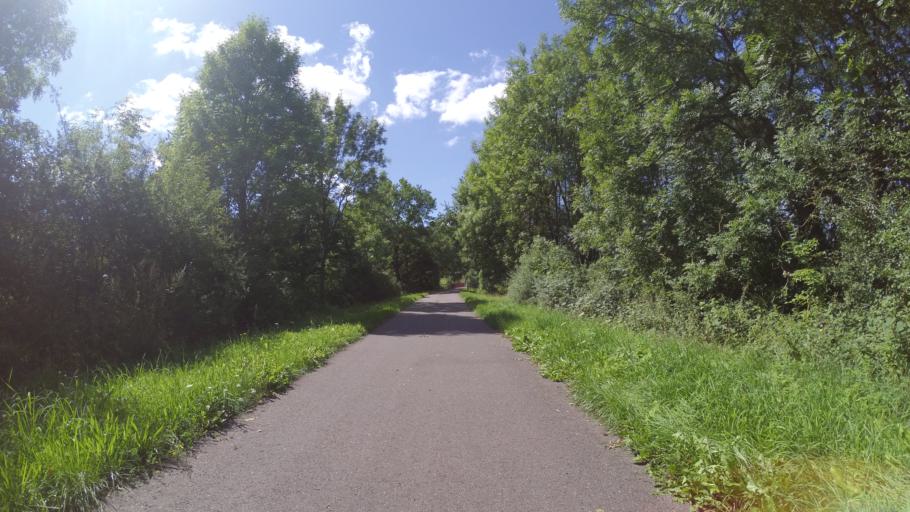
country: DE
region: Saarland
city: Oberthal
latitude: 49.5064
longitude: 7.0730
